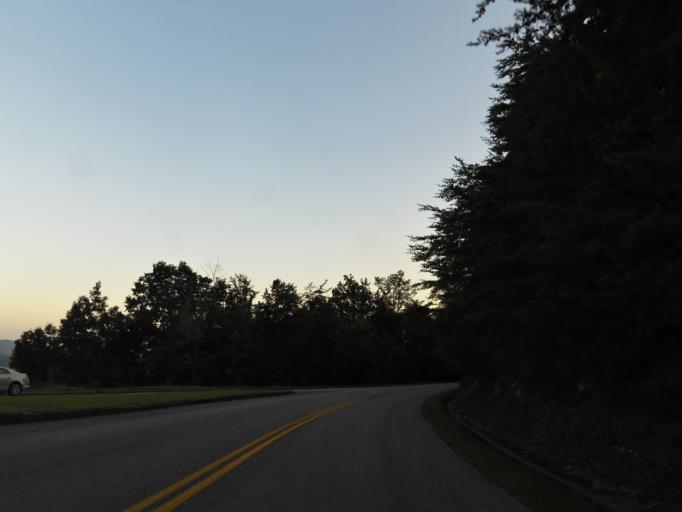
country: US
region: Tennessee
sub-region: Blount County
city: Maryville
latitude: 35.6103
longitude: -83.9765
